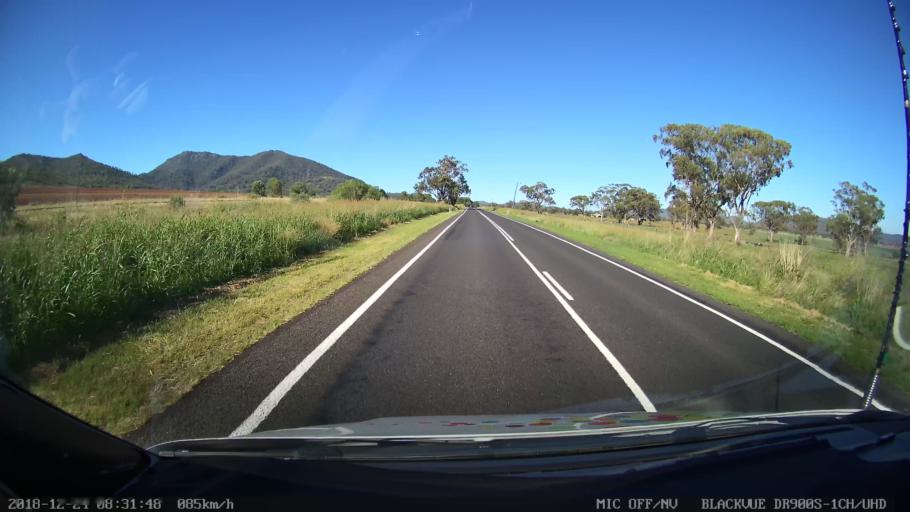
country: AU
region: New South Wales
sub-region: Tamworth Municipality
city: Phillip
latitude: -31.2759
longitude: 150.7066
